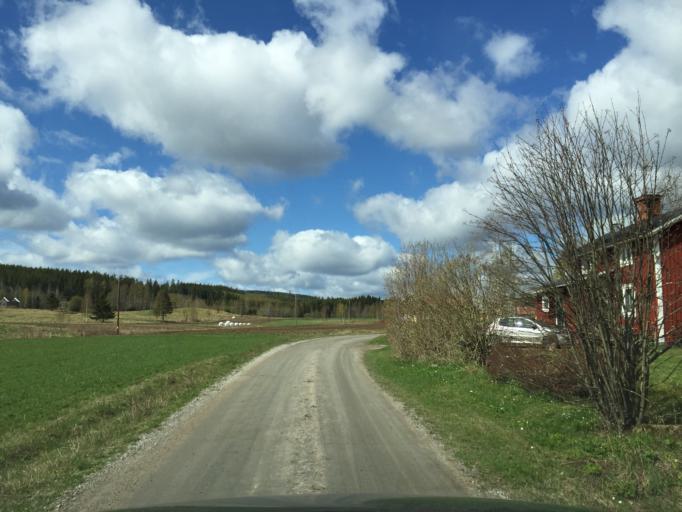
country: SE
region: Gaevleborg
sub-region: Bollnas Kommun
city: Arbra
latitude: 61.5210
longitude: 16.3355
